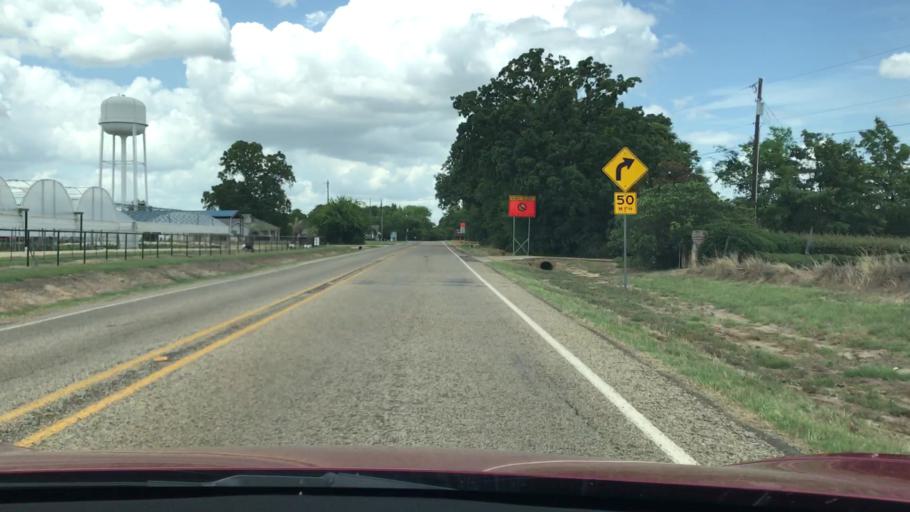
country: US
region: Texas
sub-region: Smith County
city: Hideaway
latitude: 32.4775
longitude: -95.4455
